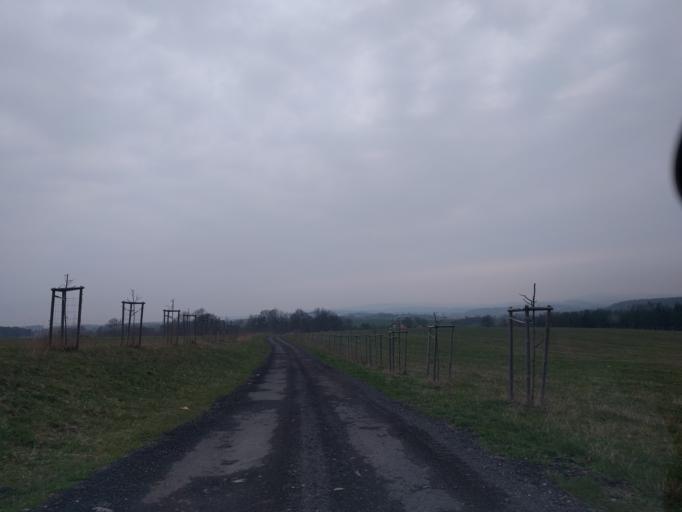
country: CZ
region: Karlovarsky
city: Bochov
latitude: 50.1121
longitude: 13.0920
